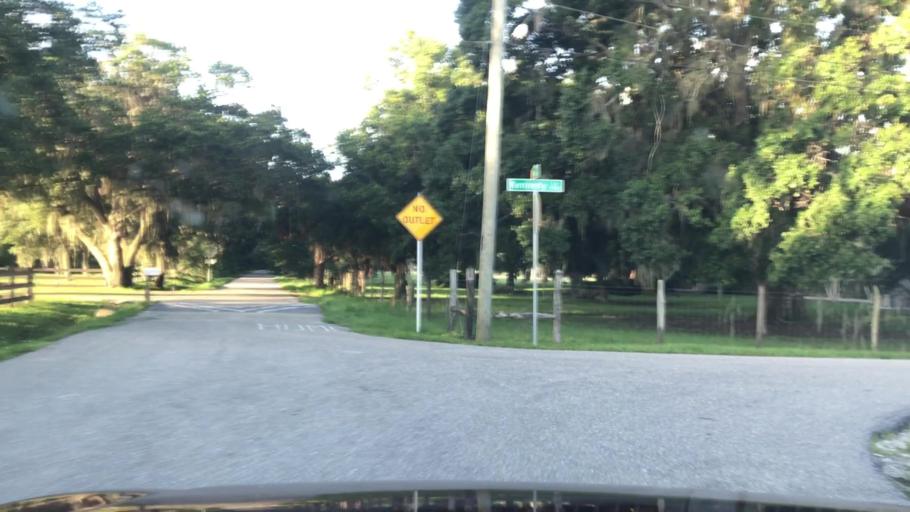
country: US
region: Florida
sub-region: Sarasota County
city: Lake Sarasota
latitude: 27.3310
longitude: -82.4083
